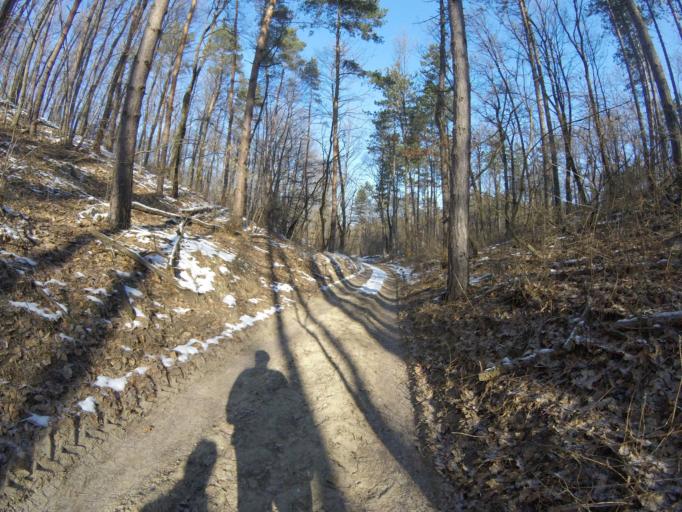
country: HU
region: Komarom-Esztergom
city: Piliscsev
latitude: 47.6644
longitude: 18.8295
